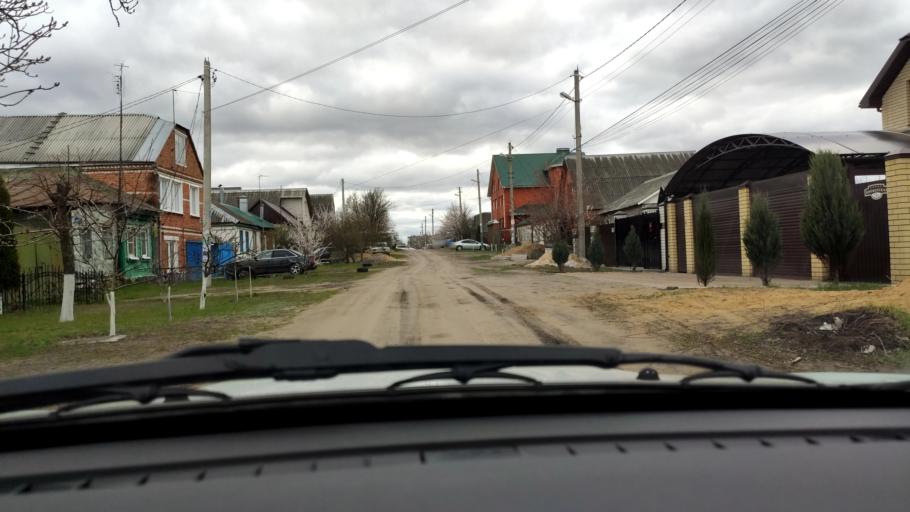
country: RU
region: Voronezj
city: Somovo
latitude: 51.7375
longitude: 39.2697
